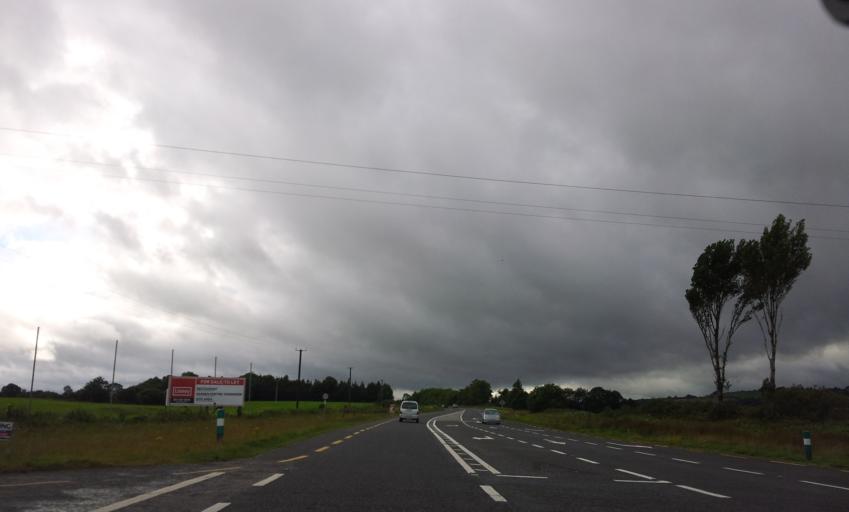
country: IE
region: Munster
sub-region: County Cork
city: Youghal
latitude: 51.9390
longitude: -7.9266
